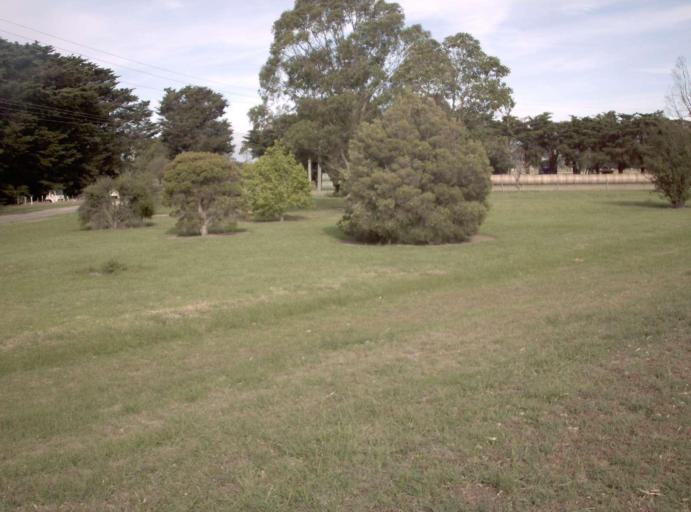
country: AU
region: Victoria
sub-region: Wellington
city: Heyfield
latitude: -38.0151
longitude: 146.7016
